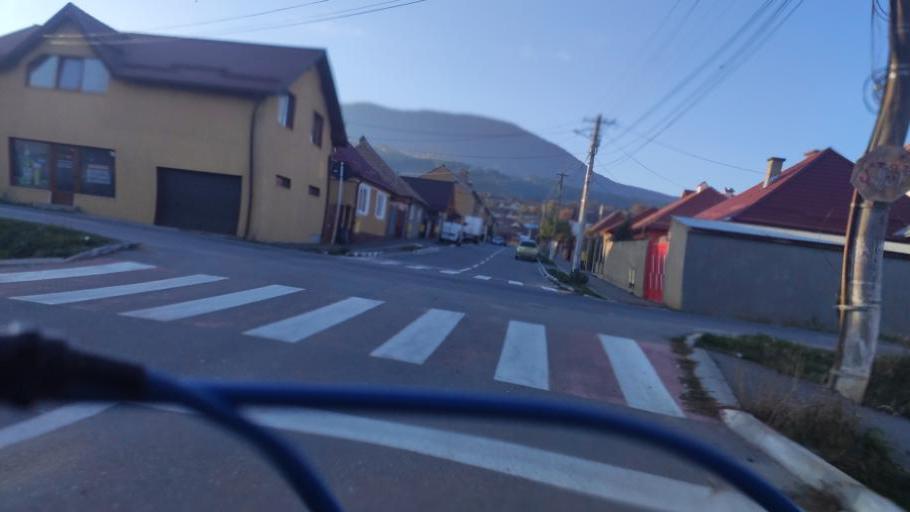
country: RO
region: Brasov
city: Codlea
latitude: 45.6906
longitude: 25.4427
